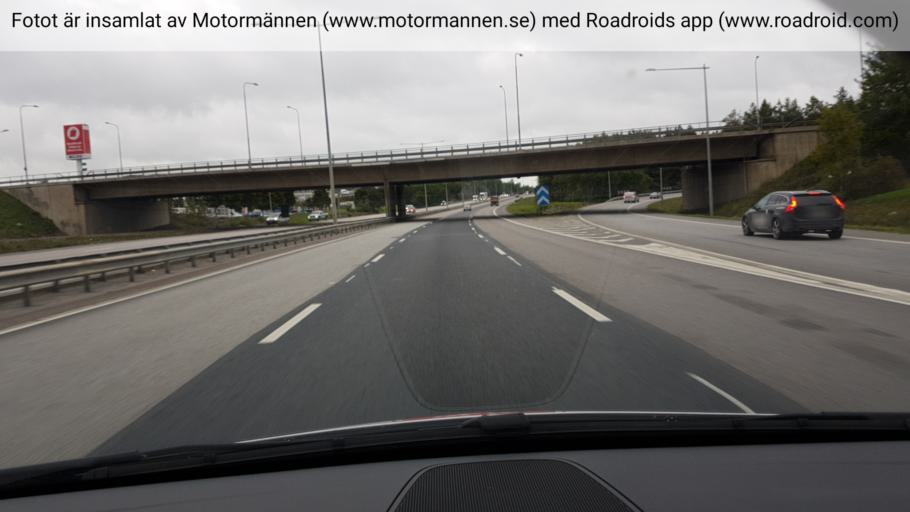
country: SE
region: Stockholm
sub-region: Haninge Kommun
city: Handen
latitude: 59.1993
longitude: 18.1329
